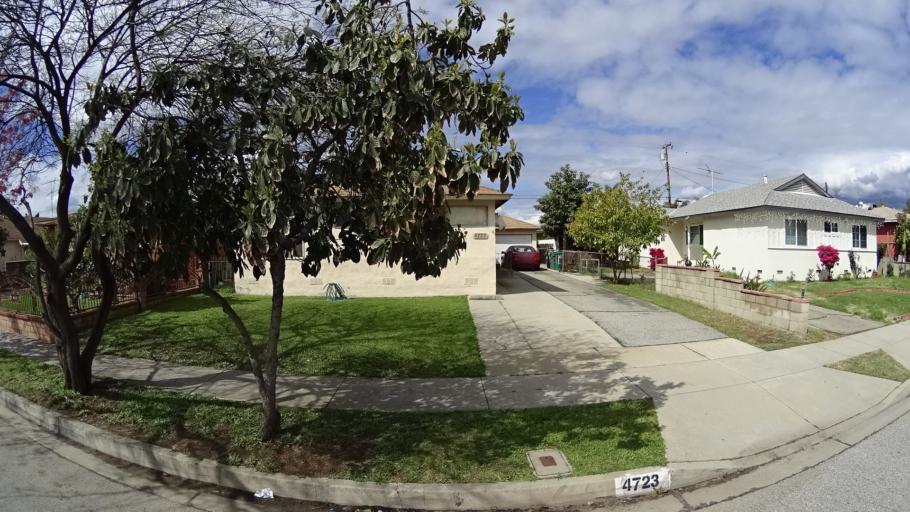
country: US
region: California
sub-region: Los Angeles County
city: Baldwin Park
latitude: 34.0984
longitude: -117.9623
